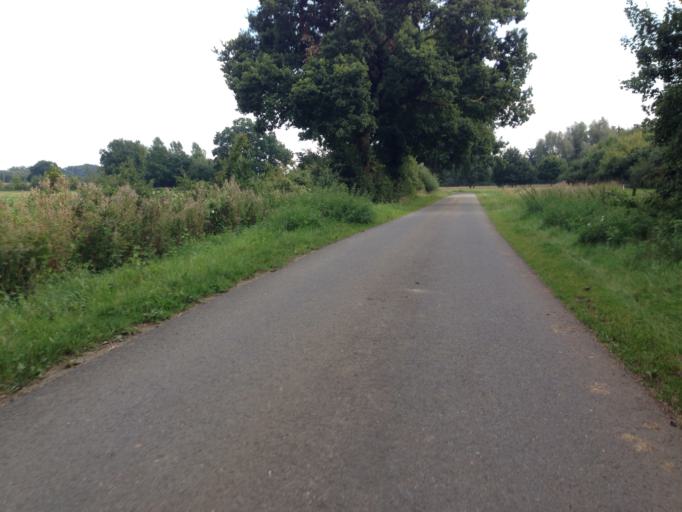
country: DE
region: North Rhine-Westphalia
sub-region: Regierungsbezirk Munster
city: Greven
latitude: 52.0215
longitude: 7.5478
